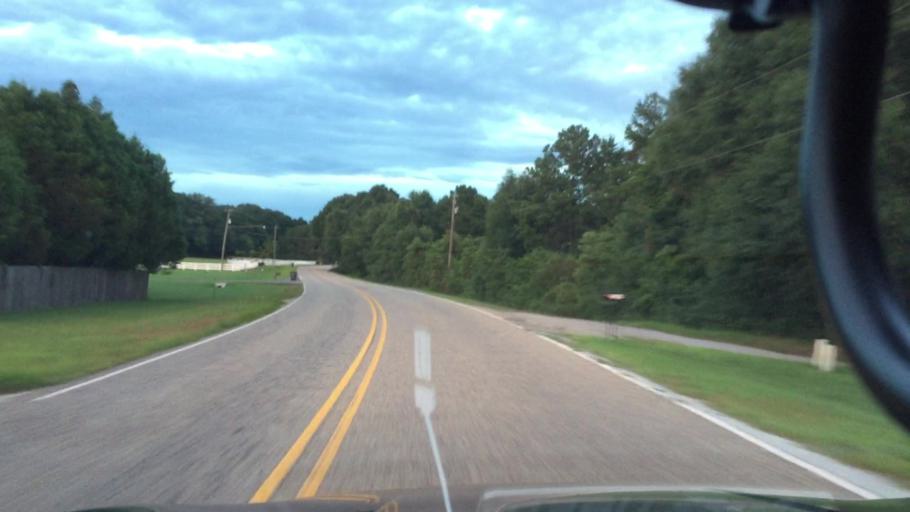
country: US
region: Alabama
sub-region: Coffee County
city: Enterprise
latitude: 31.3680
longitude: -85.8458
